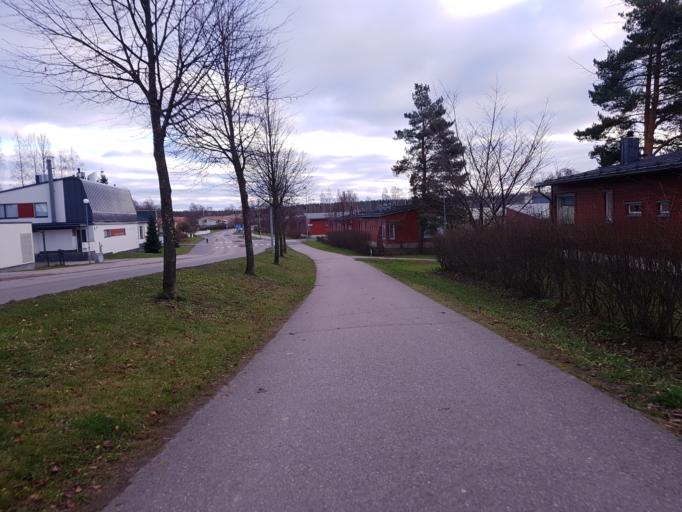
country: FI
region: Uusimaa
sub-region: Helsinki
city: Helsinki
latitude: 60.2788
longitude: 24.9095
